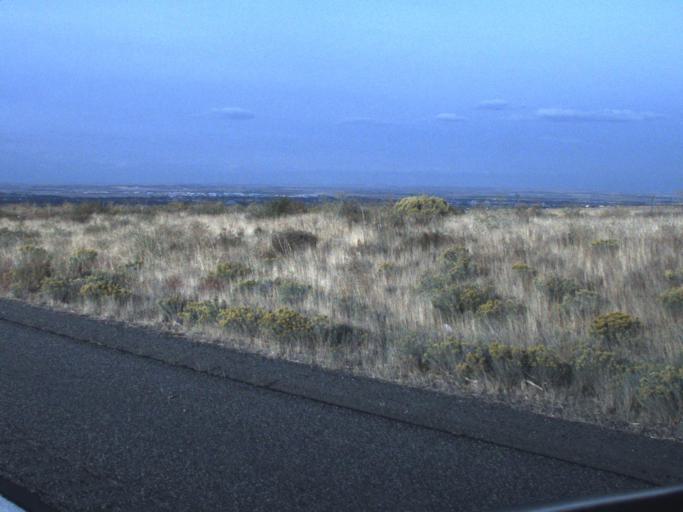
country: US
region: Washington
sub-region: Benton County
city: Kennewick
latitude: 46.1552
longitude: -119.2017
